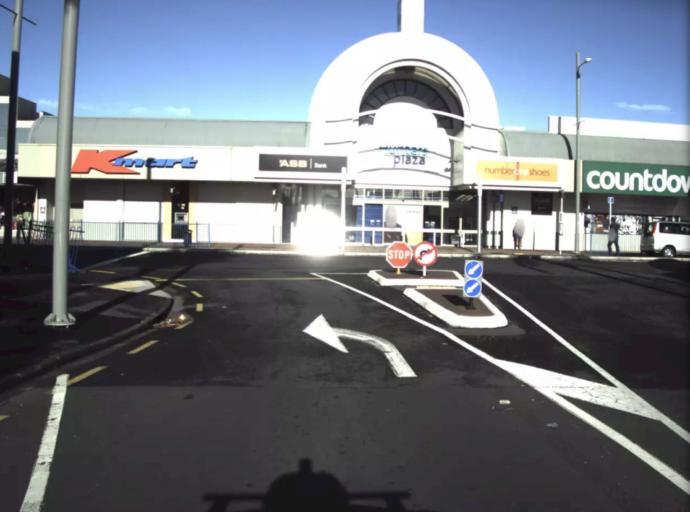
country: NZ
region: Auckland
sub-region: Auckland
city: Wiri
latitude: -36.9704
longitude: 174.8618
